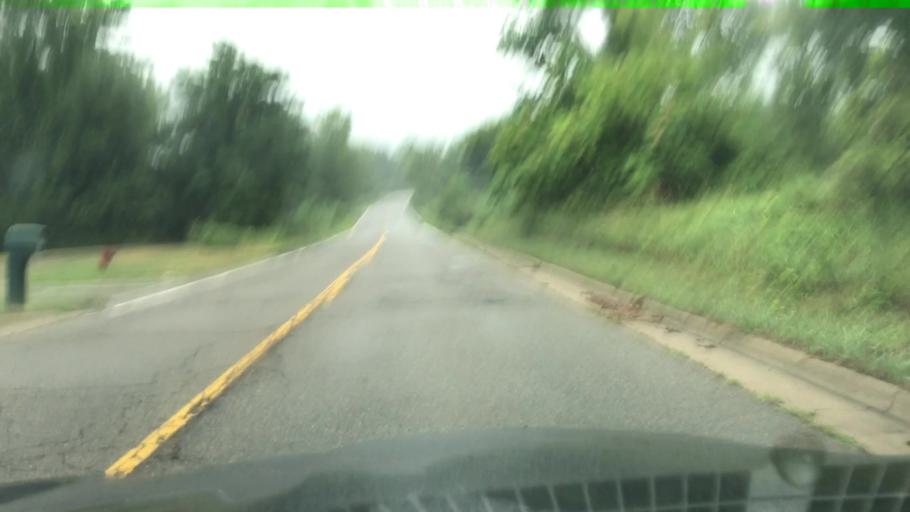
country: US
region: Michigan
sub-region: Oakland County
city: Auburn Hills
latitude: 42.7257
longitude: -83.2795
